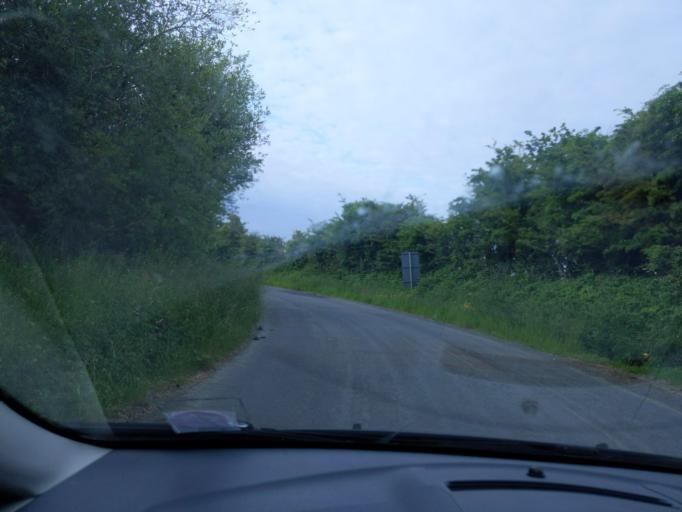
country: IM
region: Ramsey
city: Ramsey
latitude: 54.3856
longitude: -4.4498
